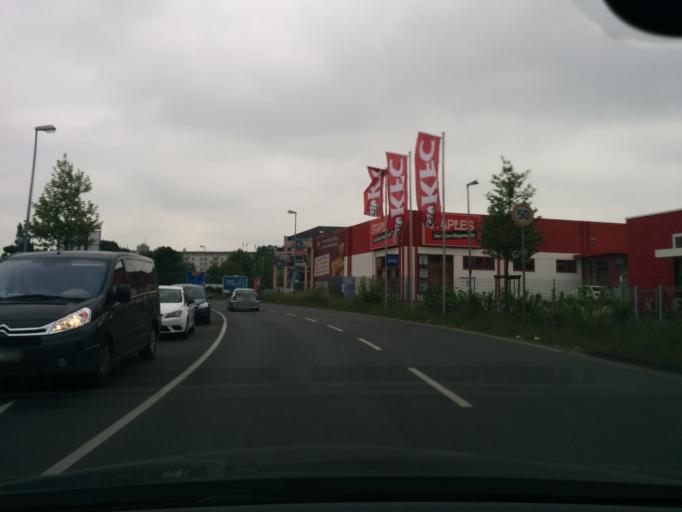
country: DE
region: North Rhine-Westphalia
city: Sankt Augustin
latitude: 50.7923
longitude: 7.1774
